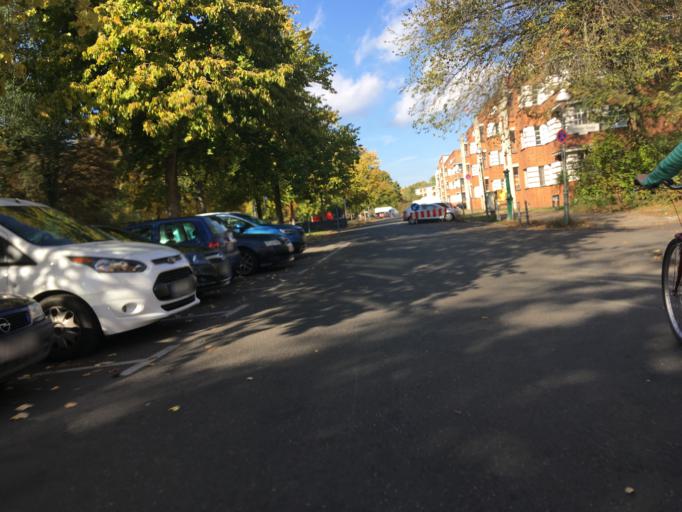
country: DE
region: Berlin
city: Wedding Bezirk
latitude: 52.5595
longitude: 13.3490
